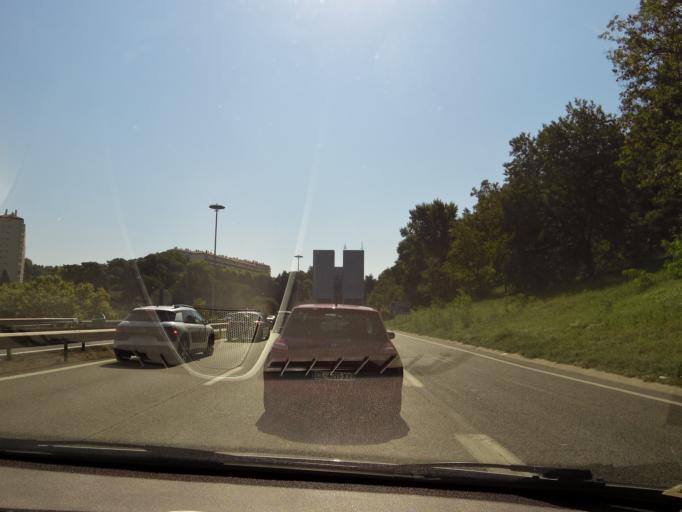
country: FR
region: Rhone-Alpes
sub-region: Departement du Rhone
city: Tassin-la-Demi-Lune
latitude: 45.7653
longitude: 4.7999
